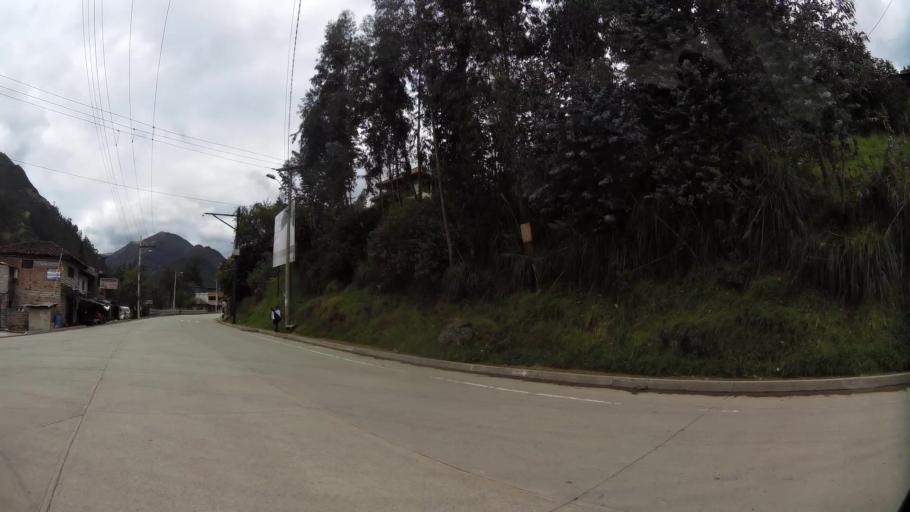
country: EC
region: Azuay
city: Cuenca
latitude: -2.8718
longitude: -79.0769
